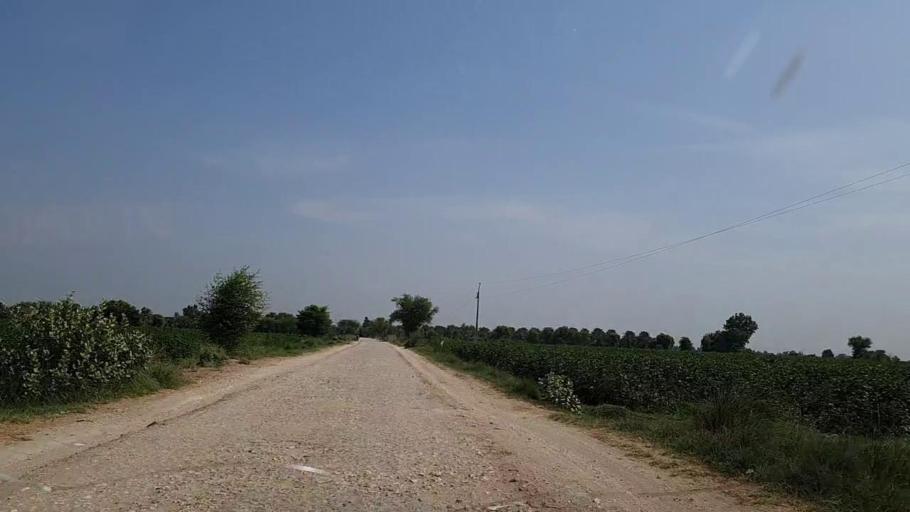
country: PK
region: Sindh
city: Khanpur
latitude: 27.7886
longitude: 69.3183
